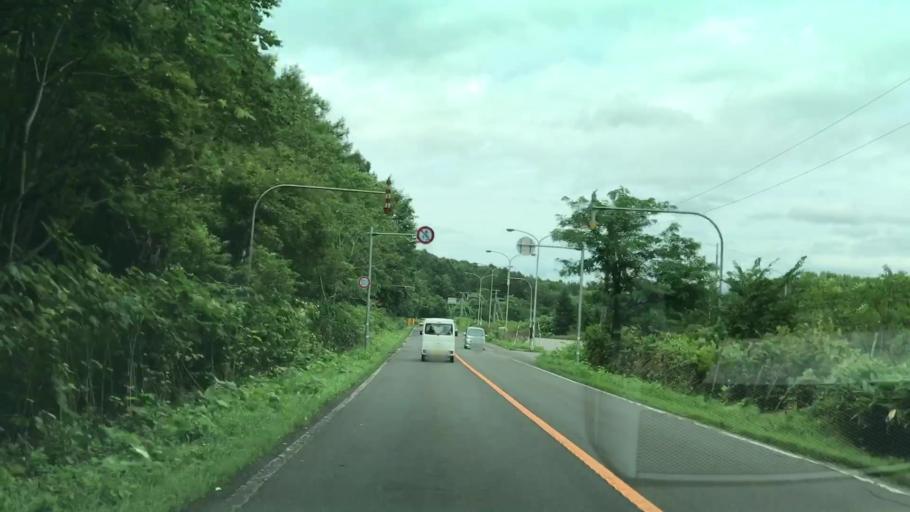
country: JP
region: Hokkaido
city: Niseko Town
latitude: 42.9495
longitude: 140.7009
